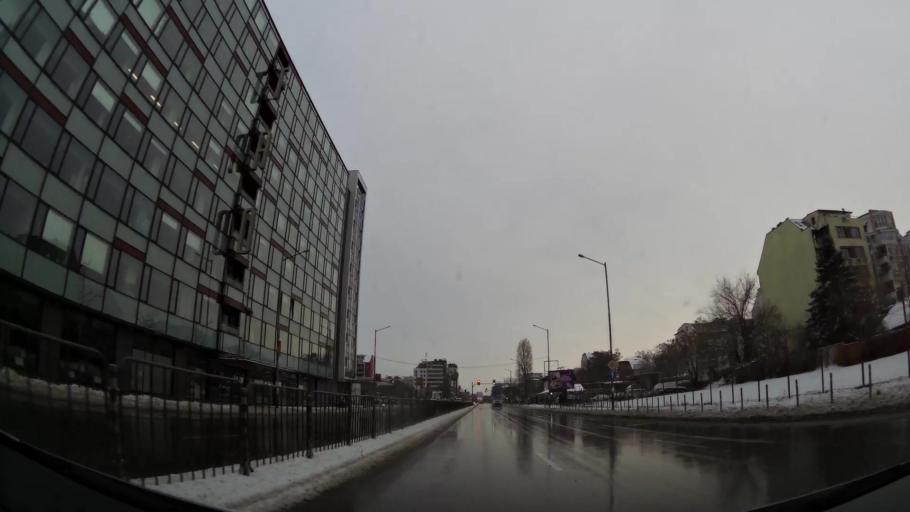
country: BG
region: Sofia-Capital
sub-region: Stolichna Obshtina
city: Sofia
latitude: 42.7006
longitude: 23.3062
